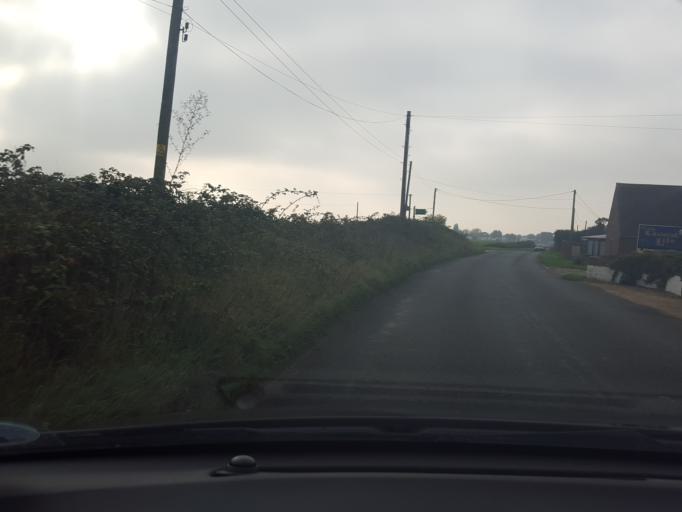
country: GB
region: England
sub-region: Essex
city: Saint Osyth
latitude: 51.7871
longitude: 1.0869
